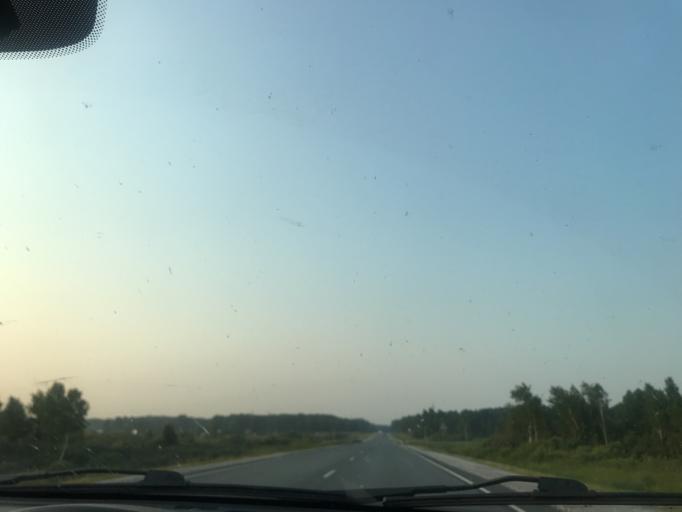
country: RU
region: Novosibirsk
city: Dorogino
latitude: 54.3730
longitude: 83.3041
